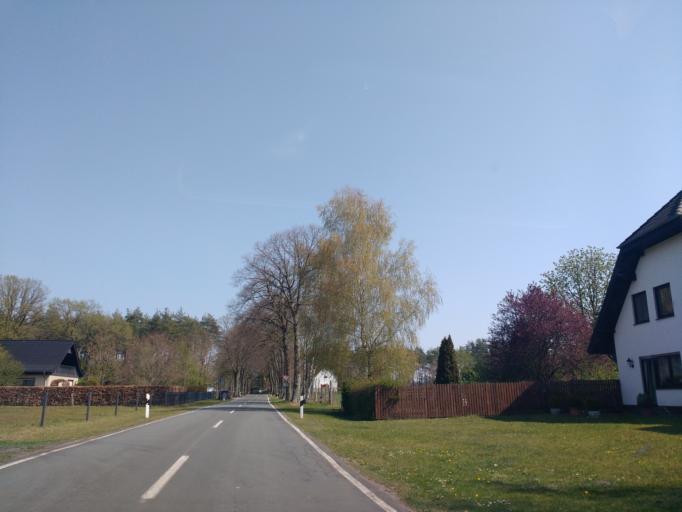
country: DE
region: North Rhine-Westphalia
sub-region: Regierungsbezirk Detmold
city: Hovelhof
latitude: 51.8342
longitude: 8.6996
